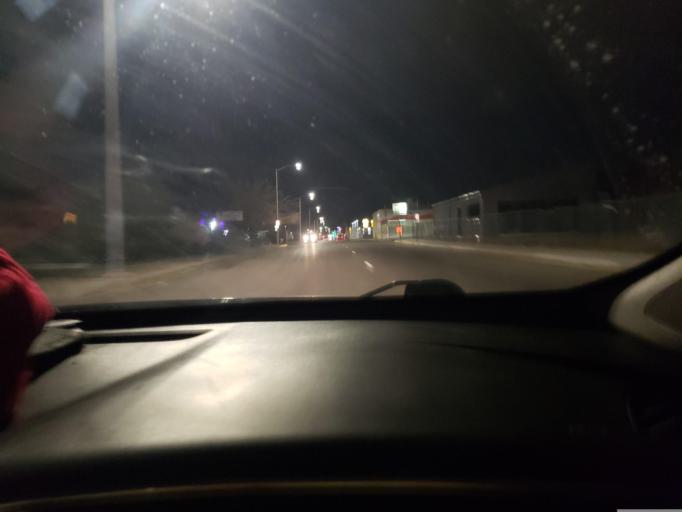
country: US
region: New Mexico
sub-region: Bernalillo County
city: Albuquerque
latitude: 35.0960
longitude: -106.6470
